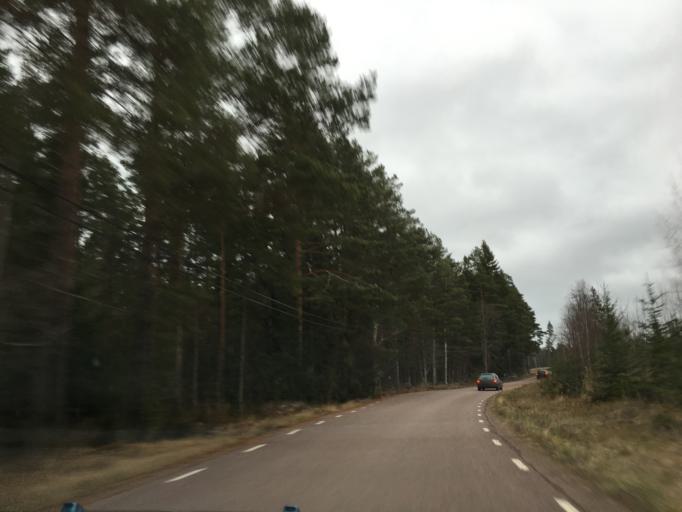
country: SE
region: Uppsala
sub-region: Alvkarleby Kommun
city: AElvkarleby
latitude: 60.6458
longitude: 17.5189
